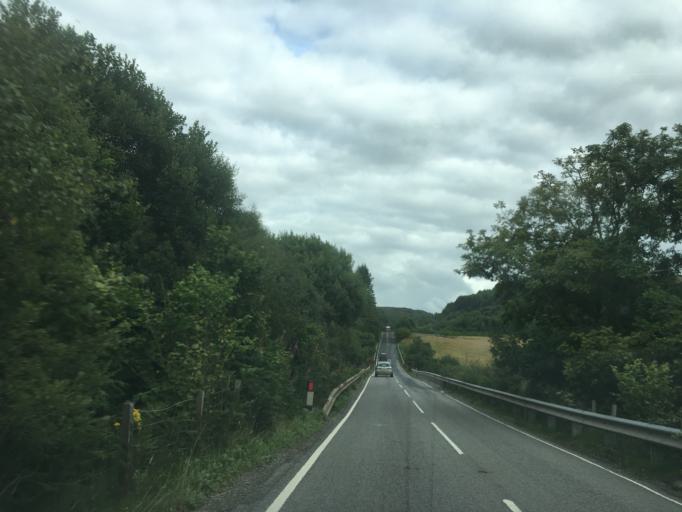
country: GB
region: Scotland
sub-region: Argyll and Bute
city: Oban
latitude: 56.3209
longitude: -5.4954
